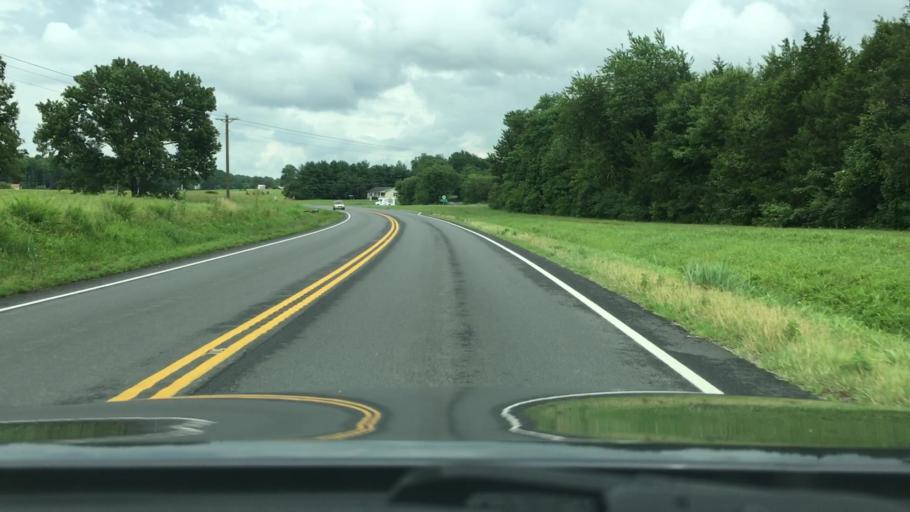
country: US
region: Virginia
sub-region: Orange County
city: Orange
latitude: 38.2715
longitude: -77.8986
